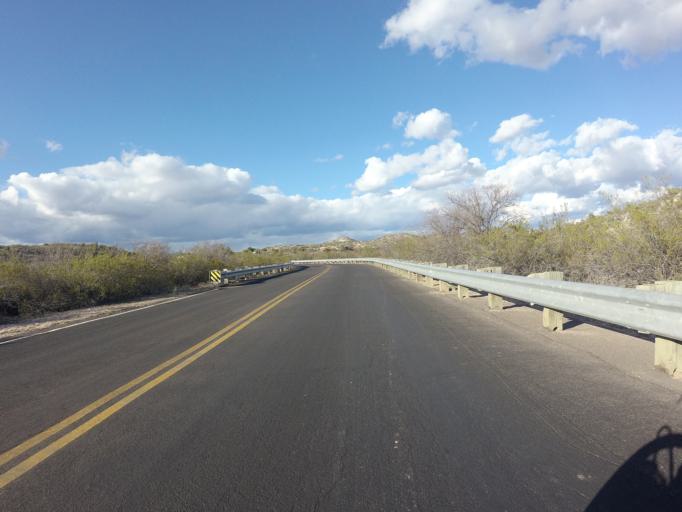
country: US
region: Arizona
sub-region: Yavapai County
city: Cottonwood
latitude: 34.7560
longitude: -112.0154
